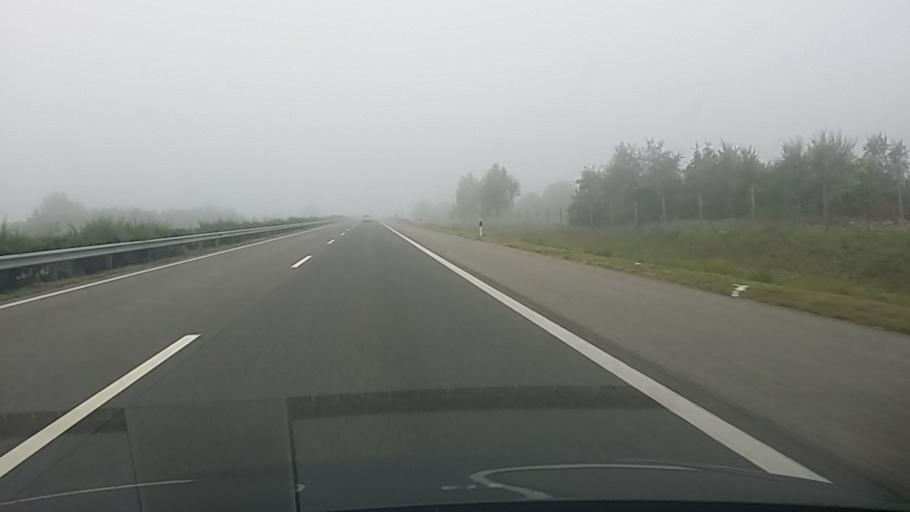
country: HU
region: Csongrad
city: Szatymaz
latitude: 46.2918
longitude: 20.0423
